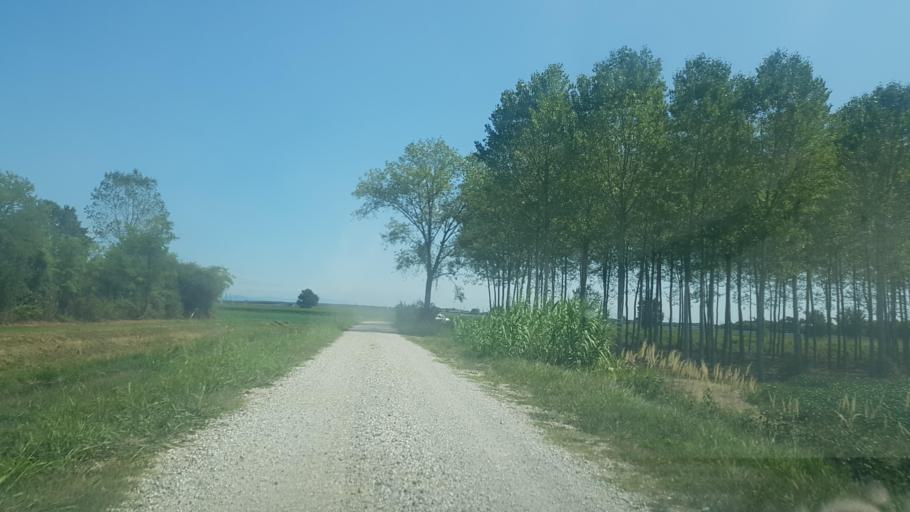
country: IT
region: Friuli Venezia Giulia
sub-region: Provincia di Udine
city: Muzzana del Turgnano
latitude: 45.8468
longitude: 13.1345
